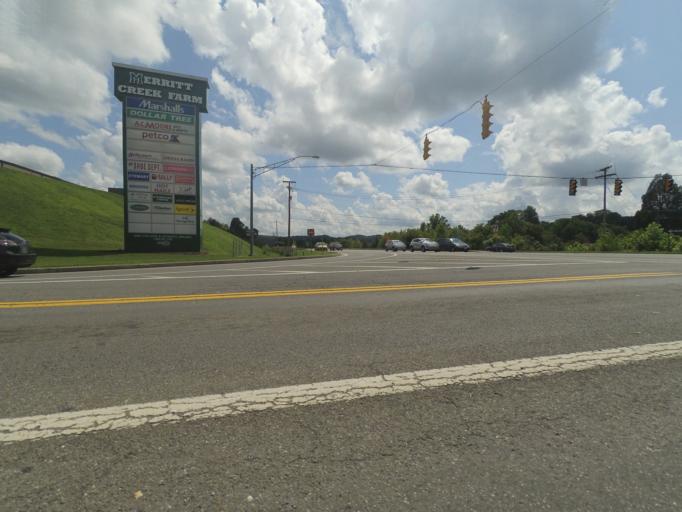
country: US
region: West Virginia
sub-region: Cabell County
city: Barboursville
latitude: 38.4226
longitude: -82.2893
